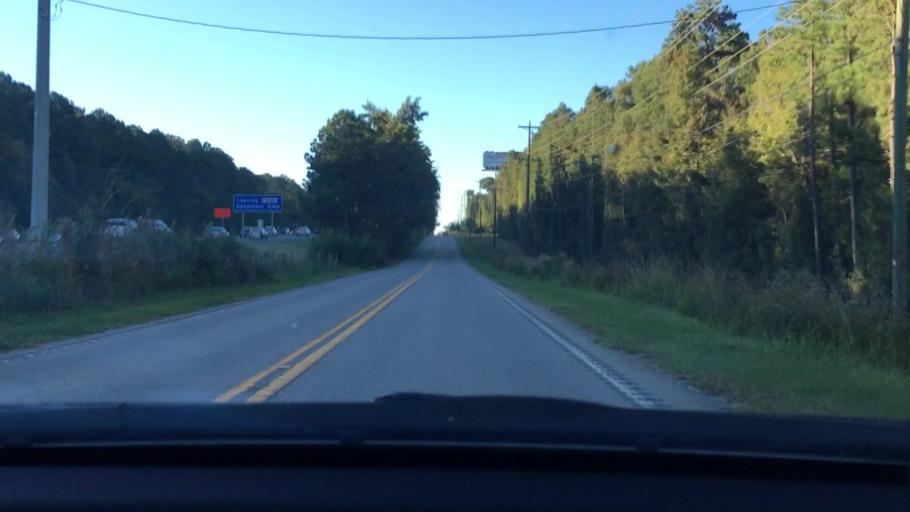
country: US
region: South Carolina
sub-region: Lexington County
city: Irmo
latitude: 34.1059
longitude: -81.1815
